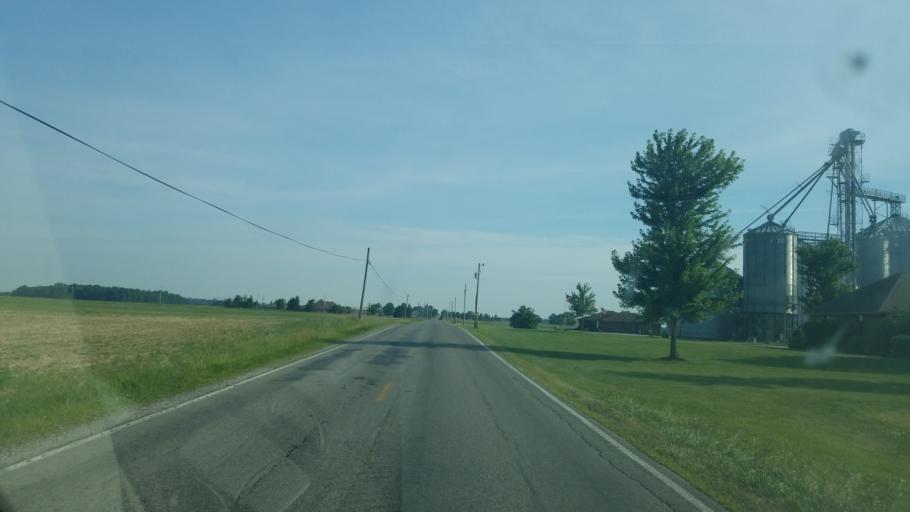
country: US
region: Ohio
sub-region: Hancock County
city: Findlay
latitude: 40.9763
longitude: -83.6985
